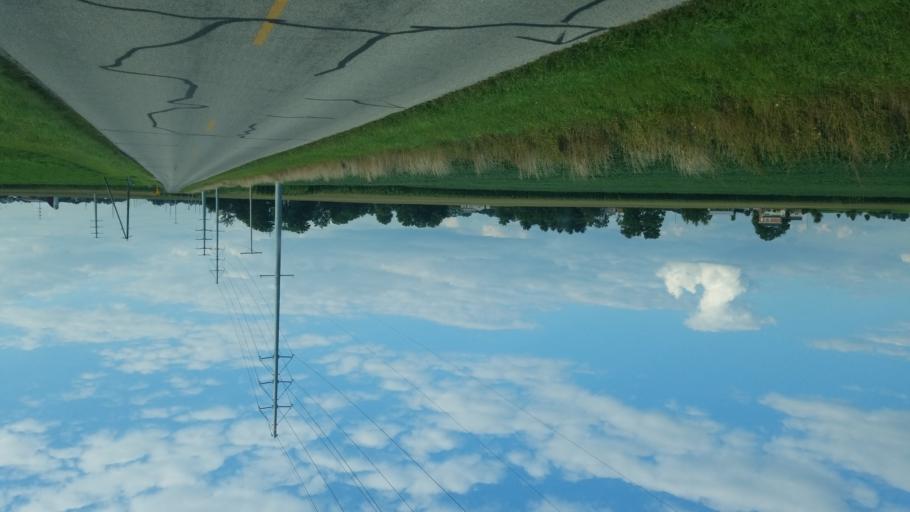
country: US
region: Ohio
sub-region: Seneca County
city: Tiffin
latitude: 41.1504
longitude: -83.1284
